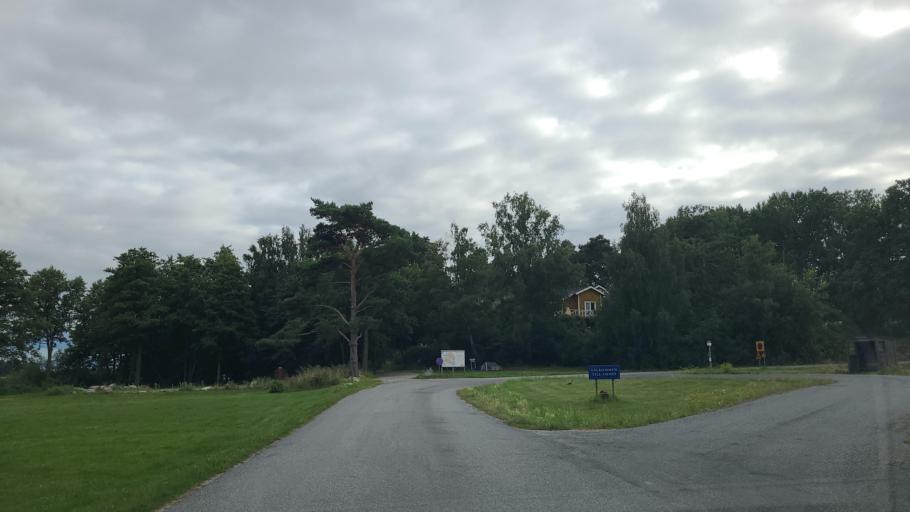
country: SE
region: Stockholm
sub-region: Upplands-Bro Kommun
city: Bro
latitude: 59.4760
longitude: 17.5610
